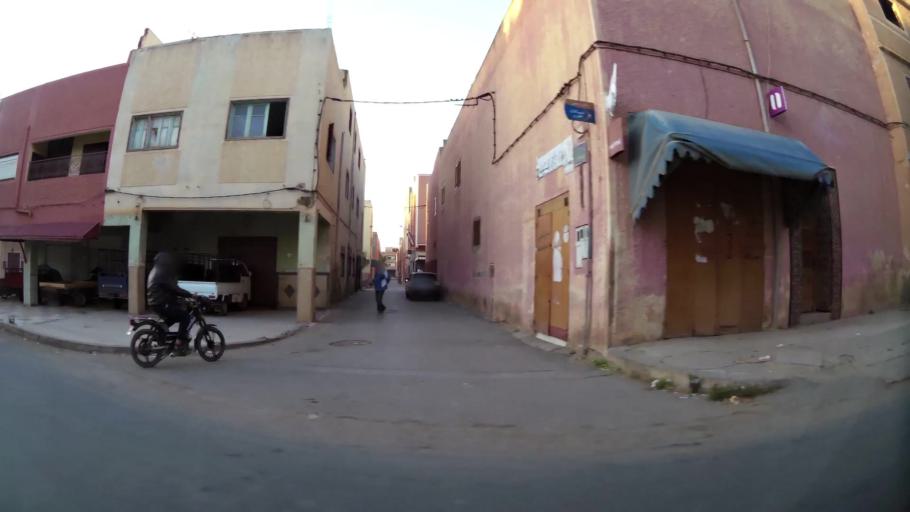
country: MA
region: Oriental
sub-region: Berkane-Taourirt
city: Berkane
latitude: 34.9189
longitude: -2.3283
